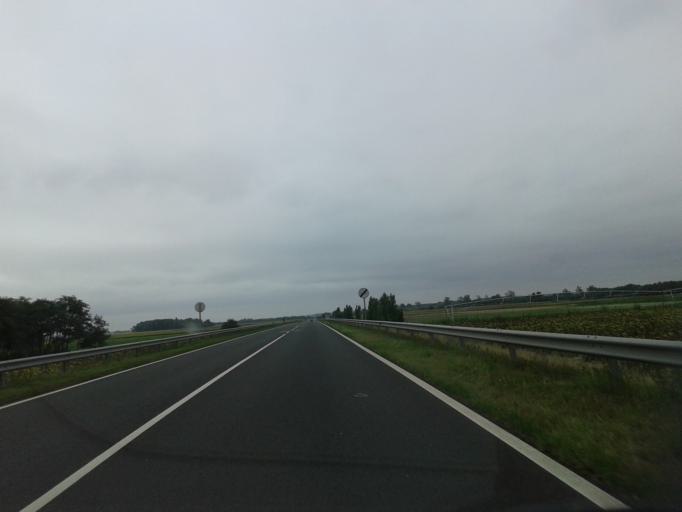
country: HU
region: Bacs-Kiskun
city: Apostag
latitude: 46.8862
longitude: 18.9826
